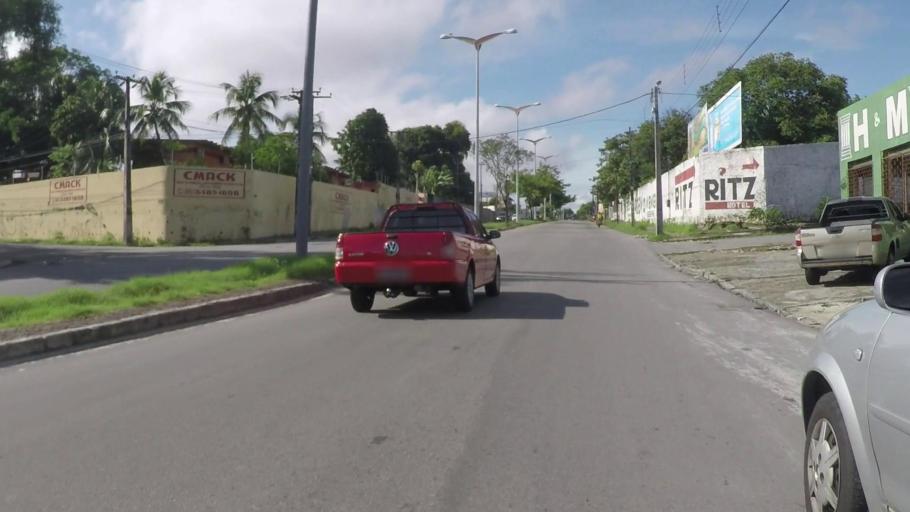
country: BR
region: Ceara
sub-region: Fortaleza
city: Fortaleza
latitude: -3.7033
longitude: -38.5916
